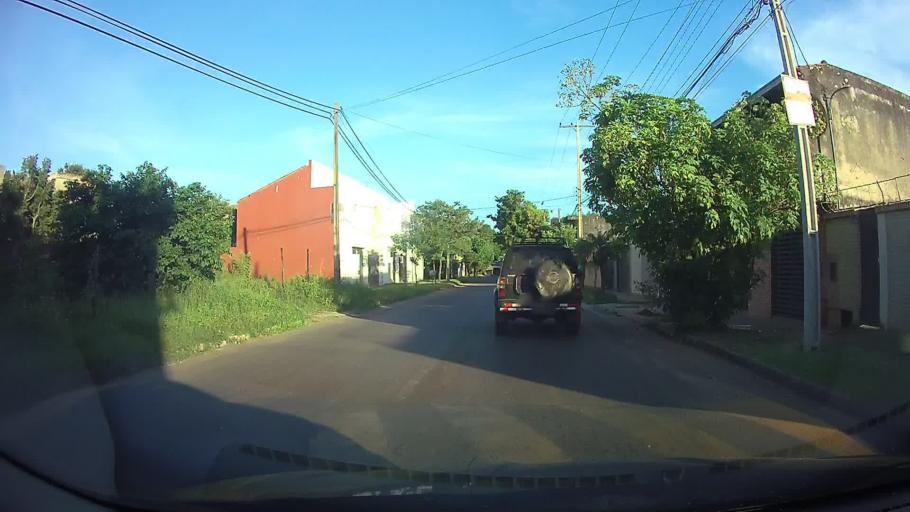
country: PY
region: Central
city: San Lorenzo
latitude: -25.2690
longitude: -57.5073
